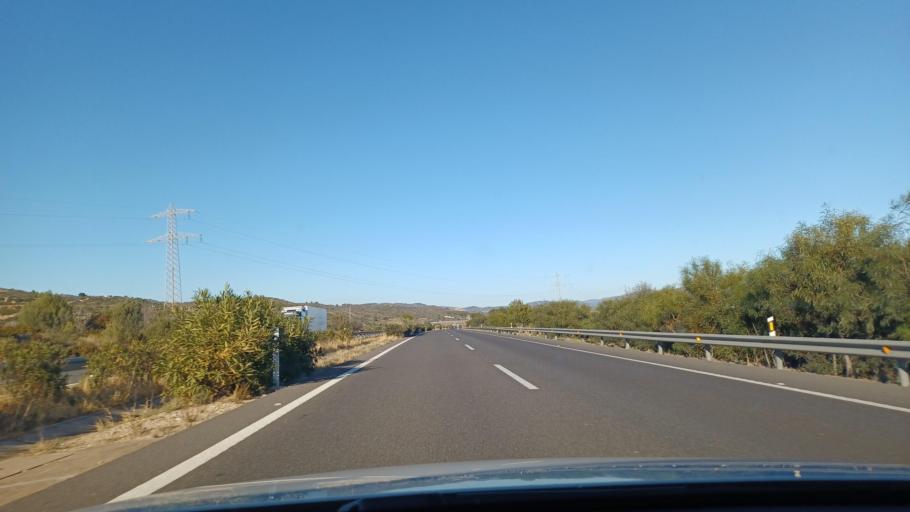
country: ES
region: Valencia
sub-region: Provincia de Castello
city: Torreblanca
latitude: 40.1750
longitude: 0.1629
